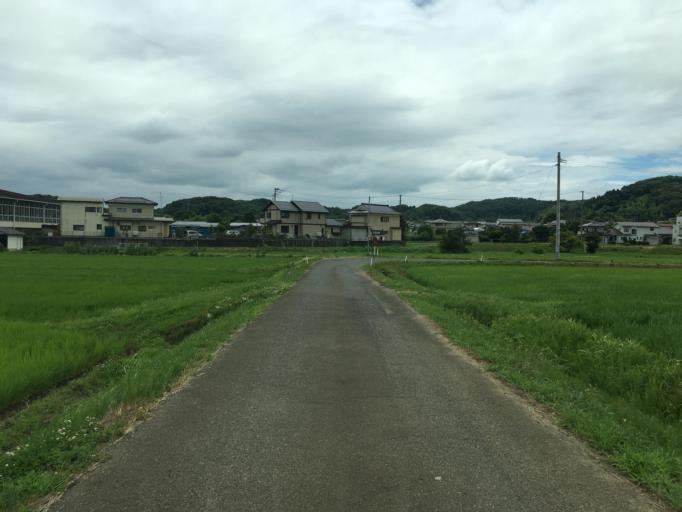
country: JP
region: Fukushima
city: Nihommatsu
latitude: 37.5627
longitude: 140.4145
